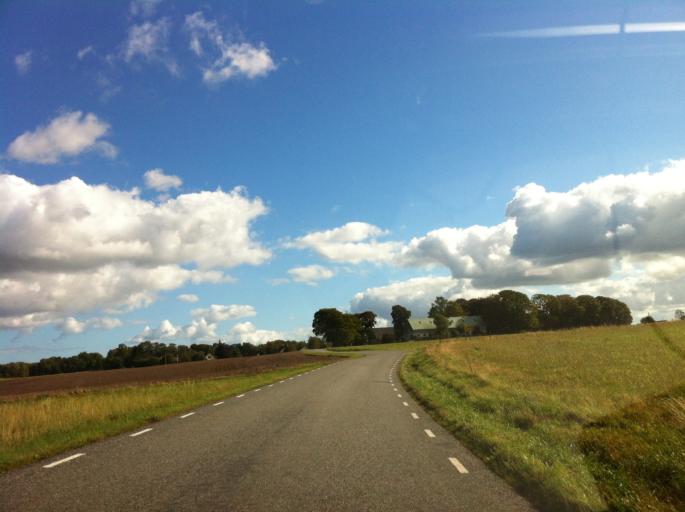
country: SE
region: Skane
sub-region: Kristianstads Kommun
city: Degeberga
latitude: 55.7029
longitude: 14.0170
